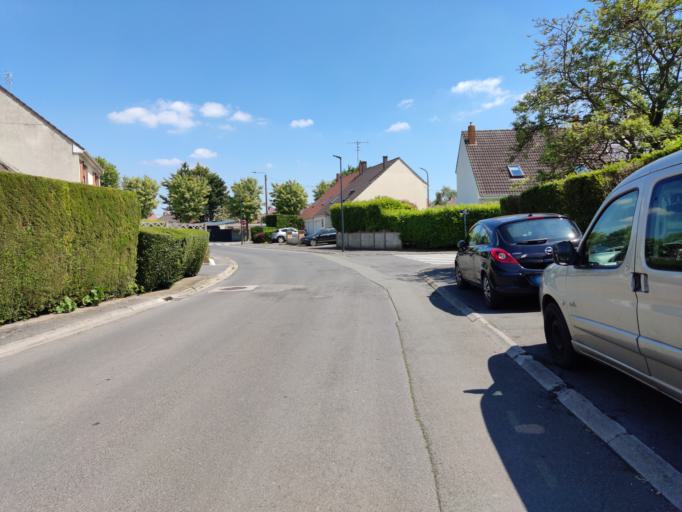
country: FR
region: Nord-Pas-de-Calais
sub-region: Departement du Pas-de-Calais
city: Henin-Beaumont
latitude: 50.4090
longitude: 2.9537
